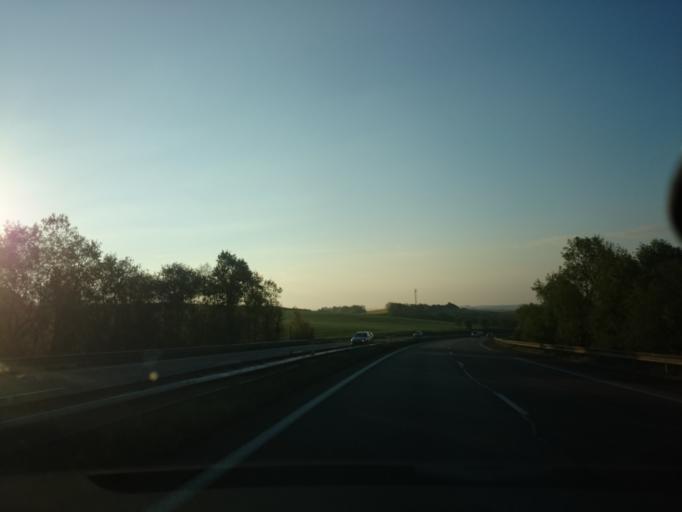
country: FR
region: Brittany
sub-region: Departement du Finistere
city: Le Faou
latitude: 48.2799
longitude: -4.1224
